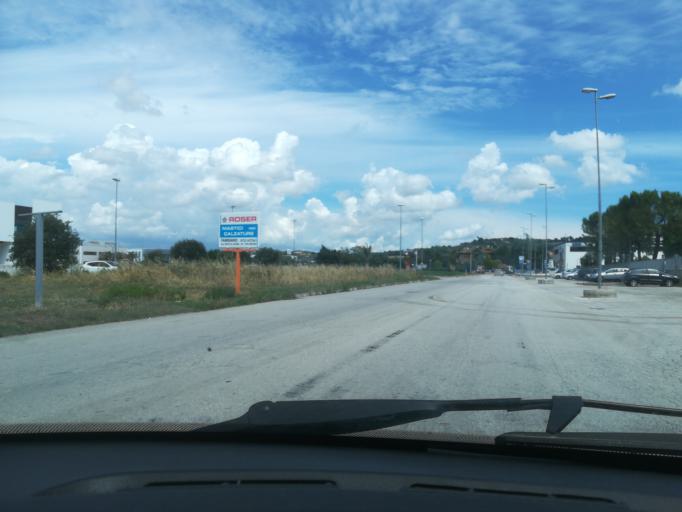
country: IT
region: The Marches
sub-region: Provincia di Macerata
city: Santa Maria Apparente
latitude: 43.2862
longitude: 13.6821
